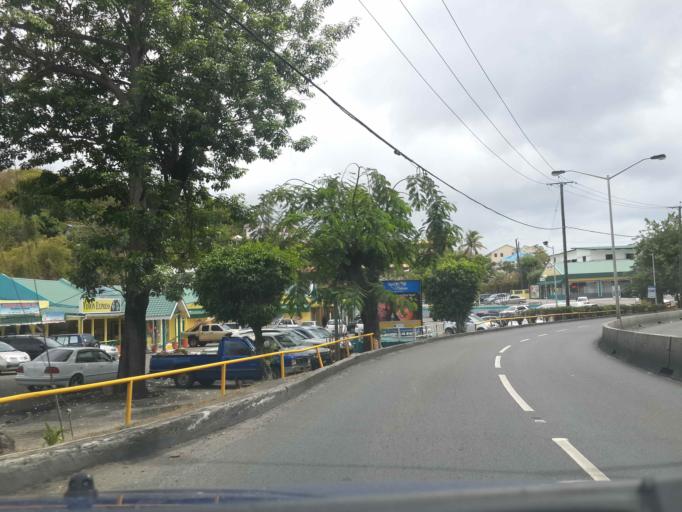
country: LC
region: Castries Quarter
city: Bisee
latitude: 14.0301
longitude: -60.9758
